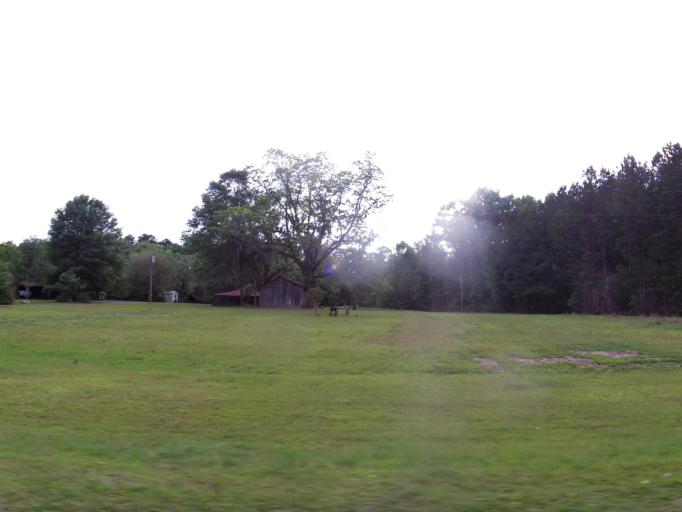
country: US
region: South Carolina
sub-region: Jasper County
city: Hardeeville
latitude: 32.3276
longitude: -81.0901
